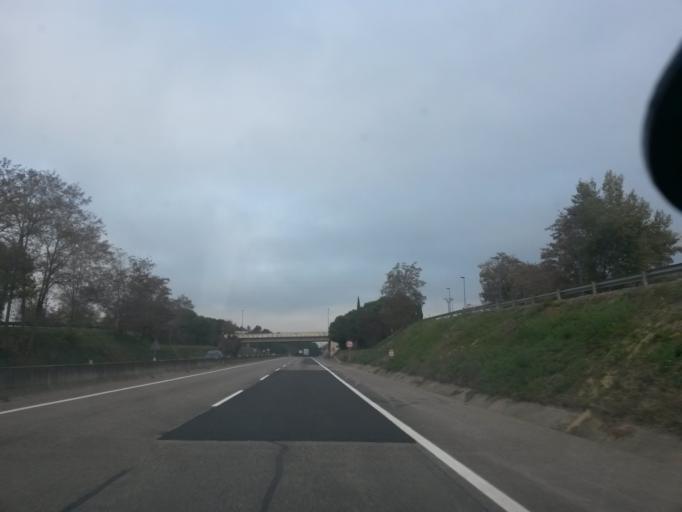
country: ES
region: Catalonia
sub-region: Provincia de Girona
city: Palol de Revardit
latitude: 42.0565
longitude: 2.8159
